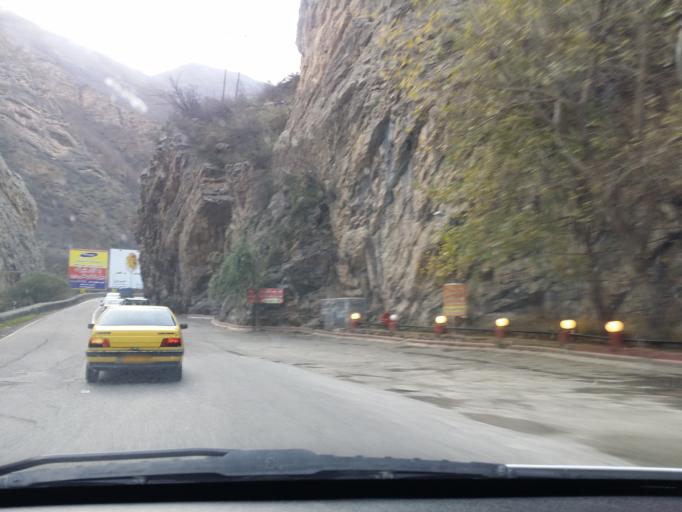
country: IR
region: Mazandaran
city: Chalus
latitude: 36.3165
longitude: 51.2470
